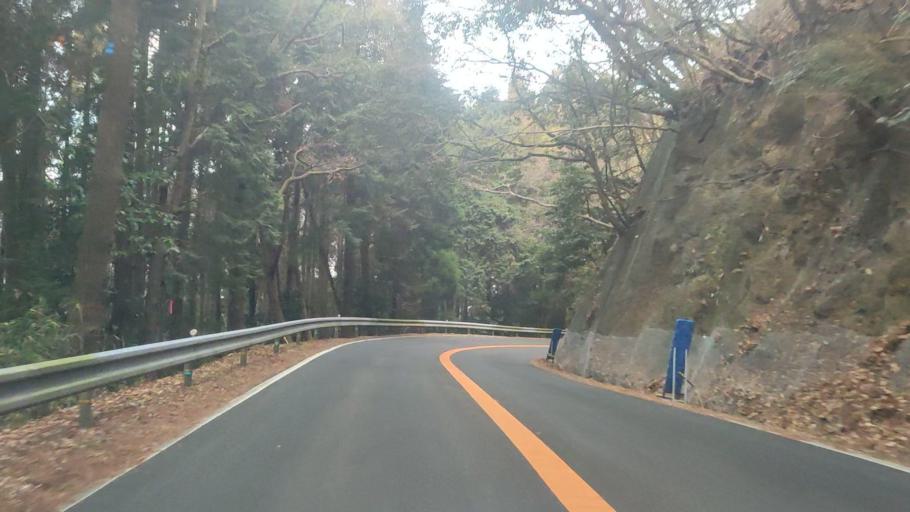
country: JP
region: Oita
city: Beppu
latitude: 33.2650
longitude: 131.3719
